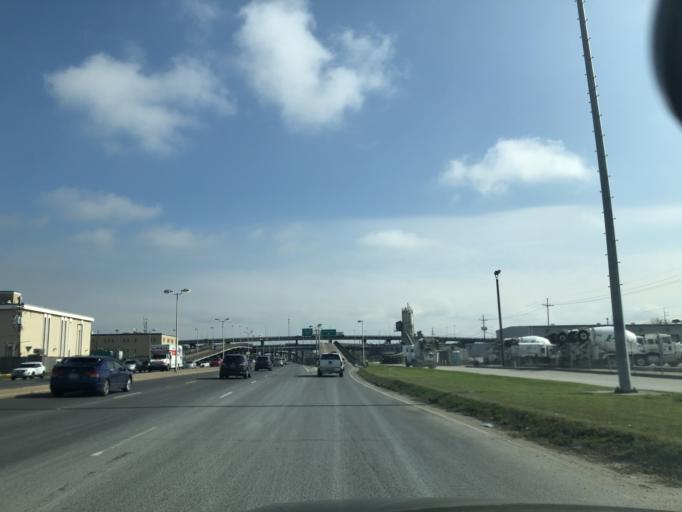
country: US
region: Louisiana
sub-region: Jefferson Parish
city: Metairie Terrace
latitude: 29.9748
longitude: -90.1603
